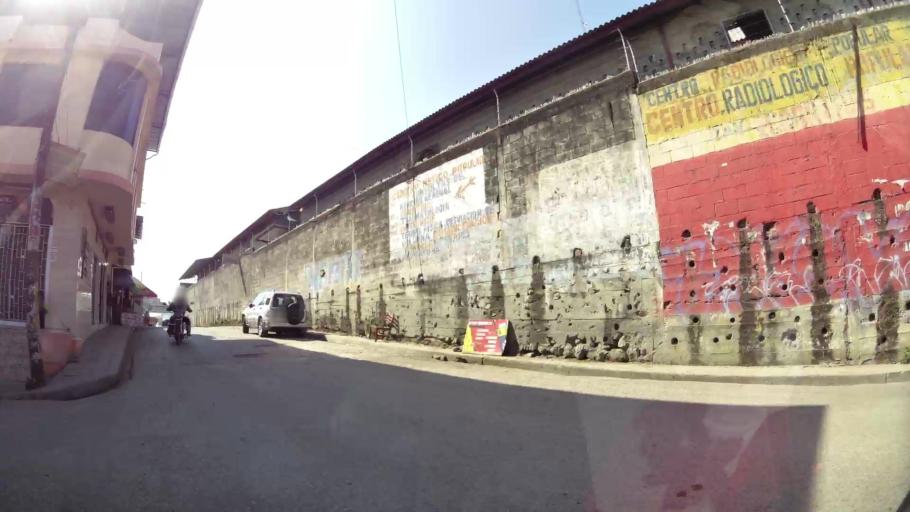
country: EC
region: Guayas
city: Santa Lucia
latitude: -2.0997
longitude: -79.9348
